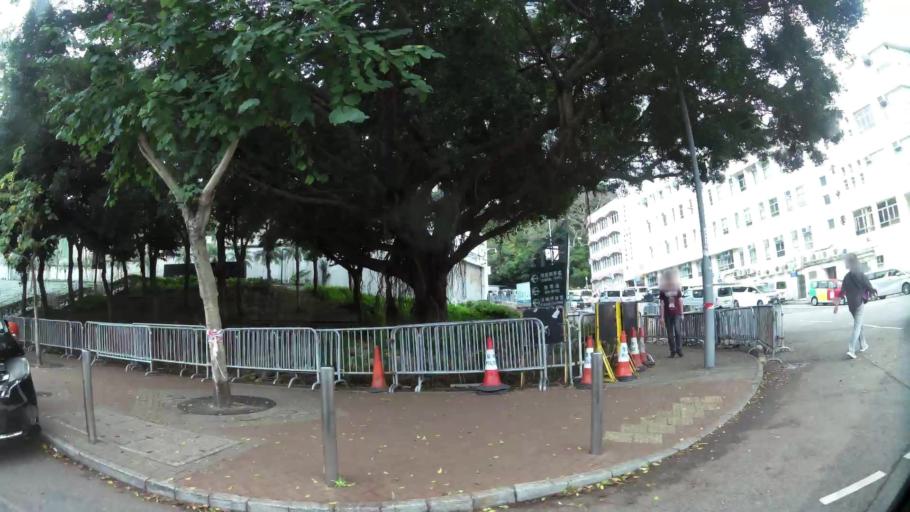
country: HK
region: Wanchai
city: Wan Chai
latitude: 22.2745
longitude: 114.1879
